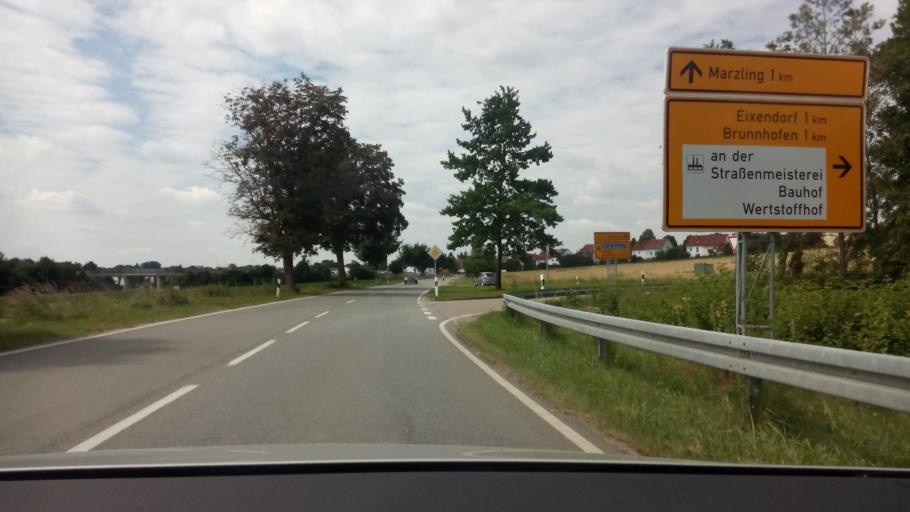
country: DE
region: Bavaria
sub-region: Upper Bavaria
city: Marzling
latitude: 48.4145
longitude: 11.8053
